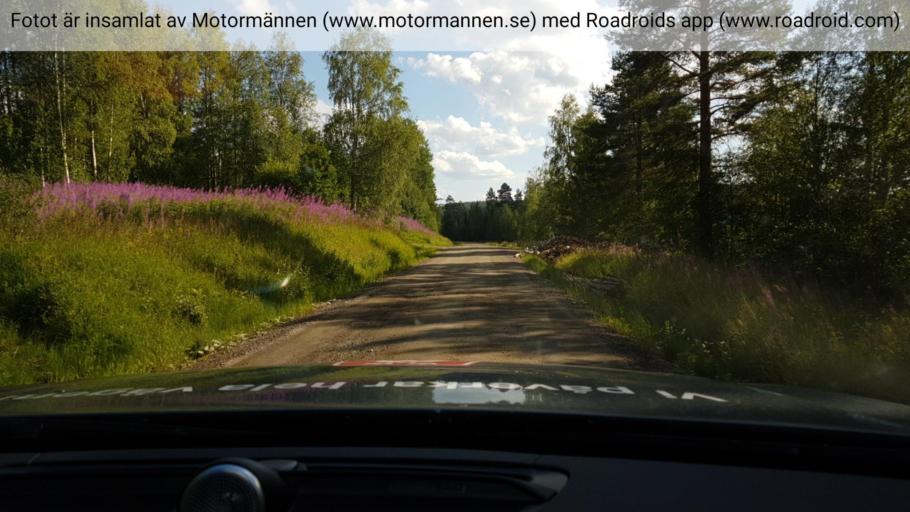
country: SE
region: Jaemtland
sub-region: Stroemsunds Kommun
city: Stroemsund
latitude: 64.0046
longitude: 15.9676
